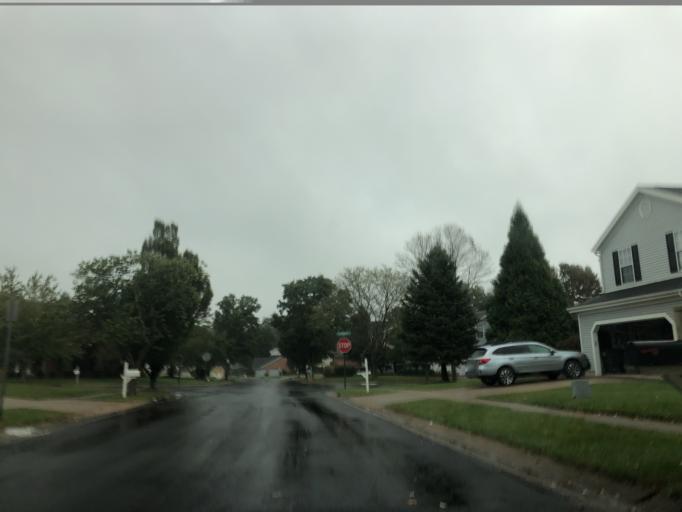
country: US
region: Ohio
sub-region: Hamilton County
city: Loveland
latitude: 39.2669
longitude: -84.2837
